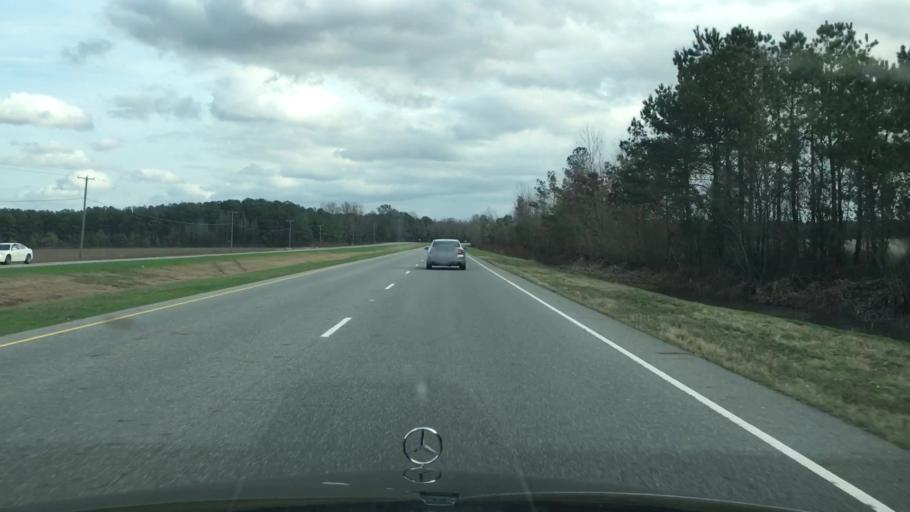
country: US
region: North Carolina
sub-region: Duplin County
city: Kenansville
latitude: 34.9485
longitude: -77.8841
